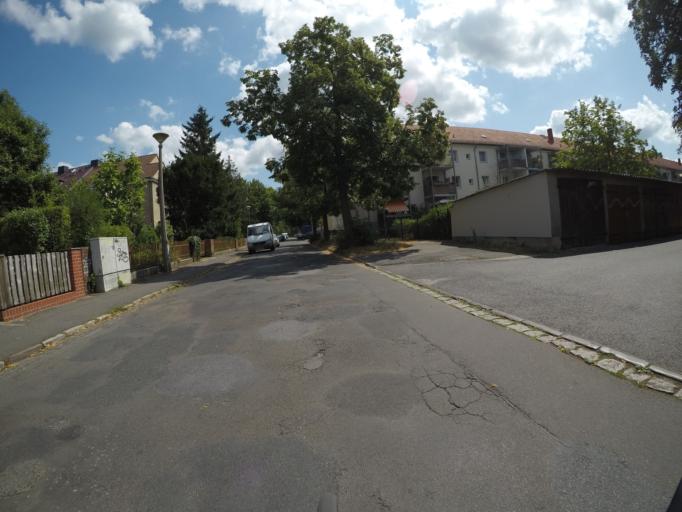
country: DE
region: Brandenburg
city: Potsdam
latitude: 52.3900
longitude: 13.1106
